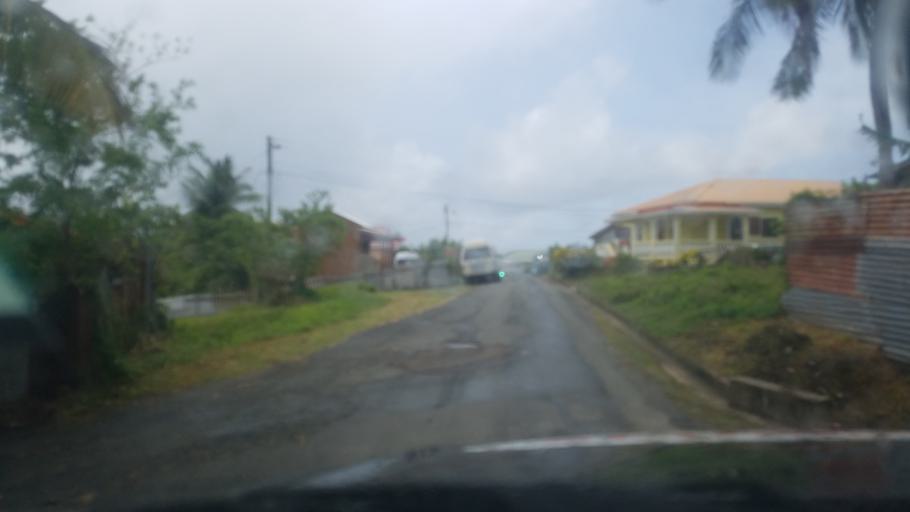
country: LC
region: Laborie Quarter
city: Laborie
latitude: 13.7470
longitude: -60.9642
